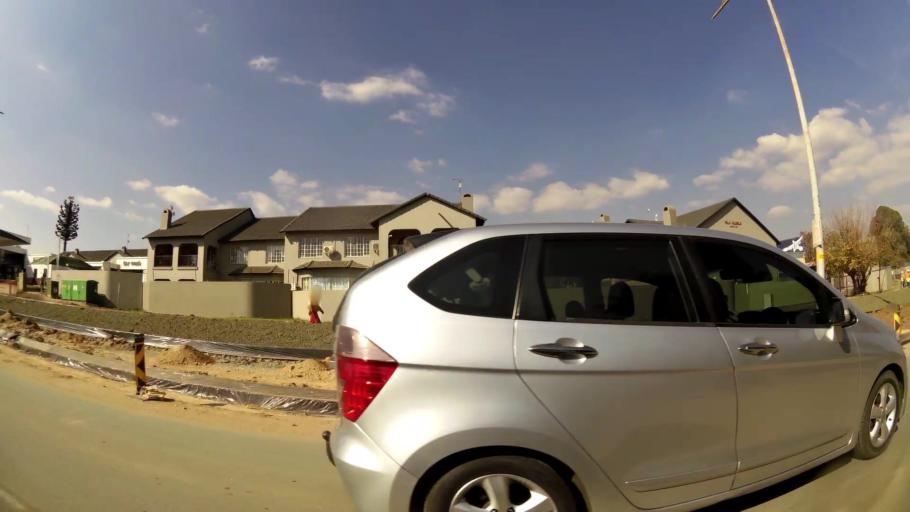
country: ZA
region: Gauteng
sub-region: Ekurhuleni Metropolitan Municipality
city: Tembisa
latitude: -26.0769
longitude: 28.2544
